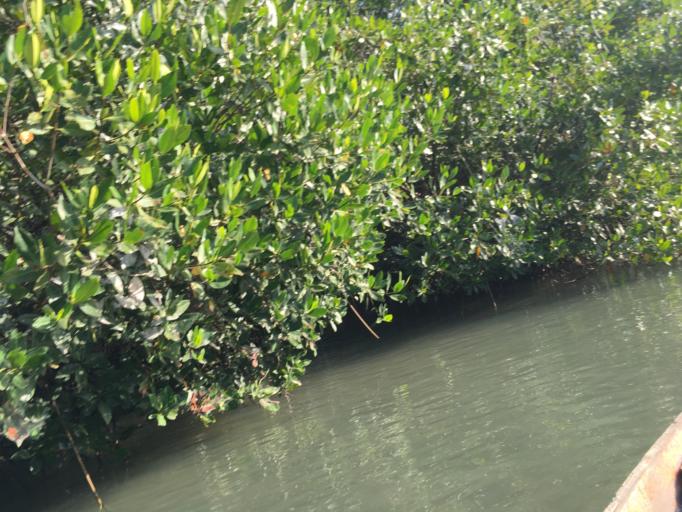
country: CO
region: Bolivar
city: Cartagena
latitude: 10.4848
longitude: -75.4839
